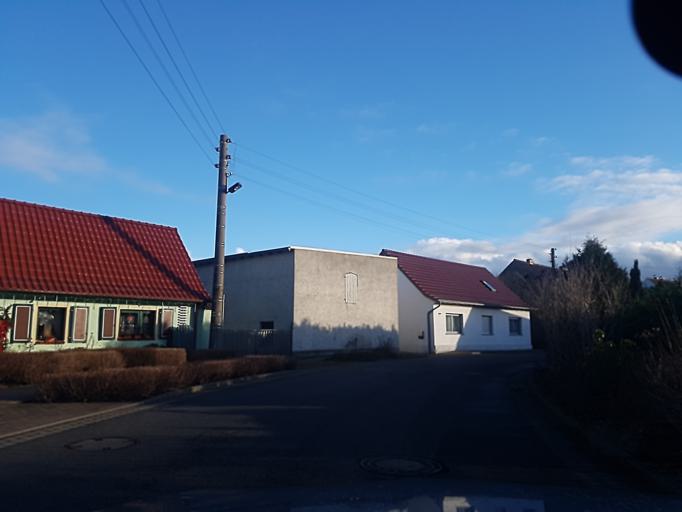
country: DE
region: Brandenburg
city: Bad Liebenwerda
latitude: 51.5531
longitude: 13.3626
